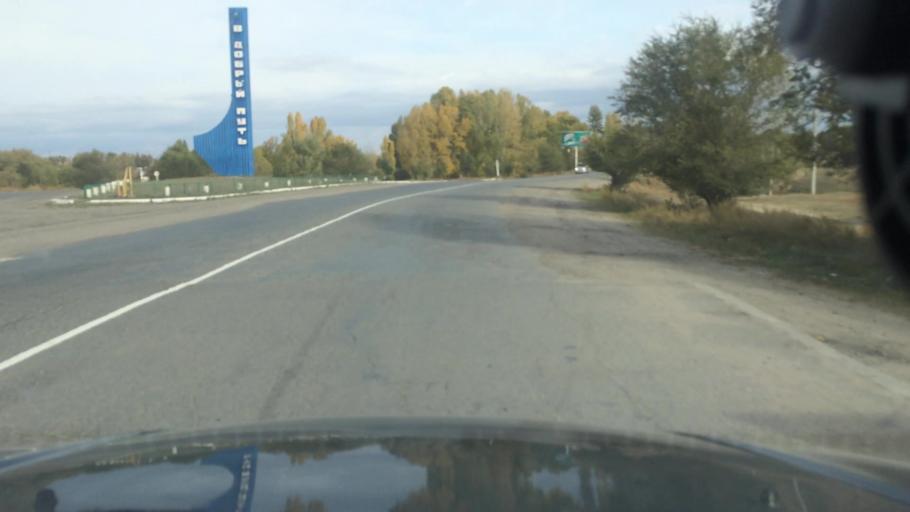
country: KG
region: Ysyk-Koel
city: Karakol
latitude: 42.5322
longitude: 78.3816
